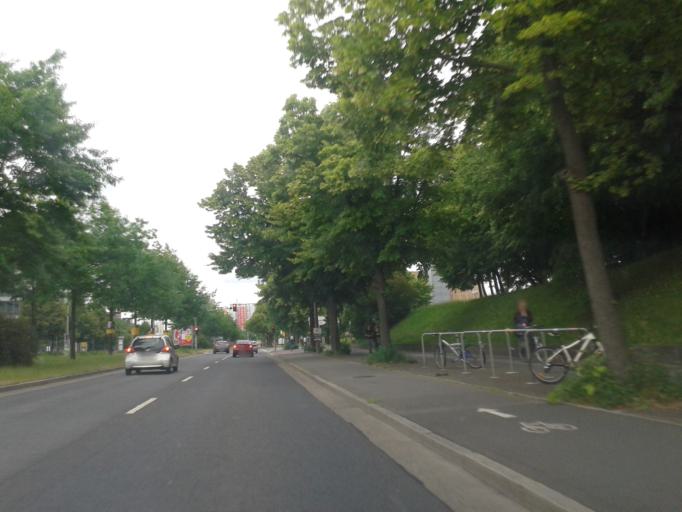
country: DE
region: Saxony
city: Dresden
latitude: 51.0291
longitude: 13.7369
